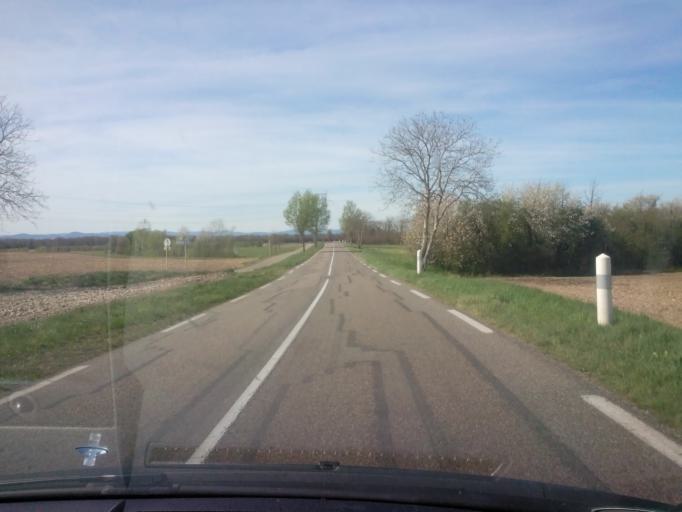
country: FR
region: Alsace
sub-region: Departement du Haut-Rhin
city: Fessenheim
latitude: 47.9441
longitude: 7.5429
